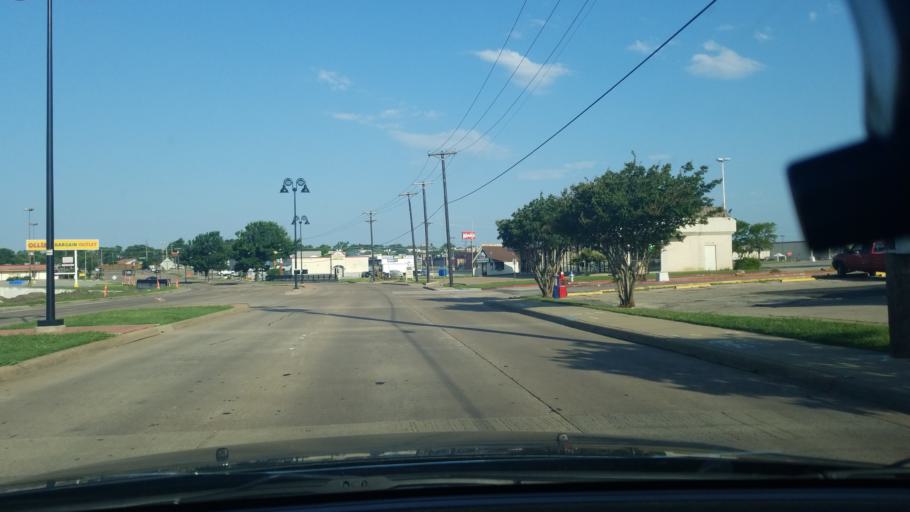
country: US
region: Texas
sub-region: Dallas County
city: Mesquite
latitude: 32.8115
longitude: -96.6307
